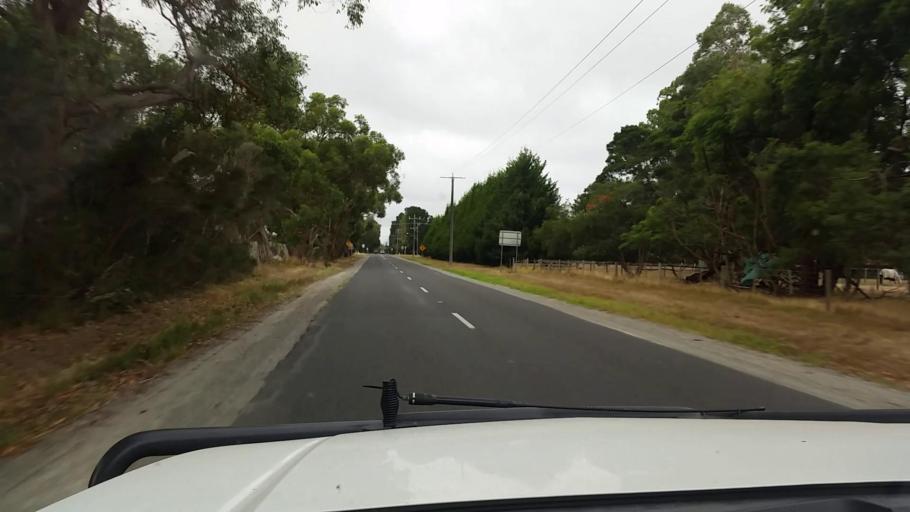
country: AU
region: Victoria
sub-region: Mornington Peninsula
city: Balnarring
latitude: -38.3411
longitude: 145.1457
